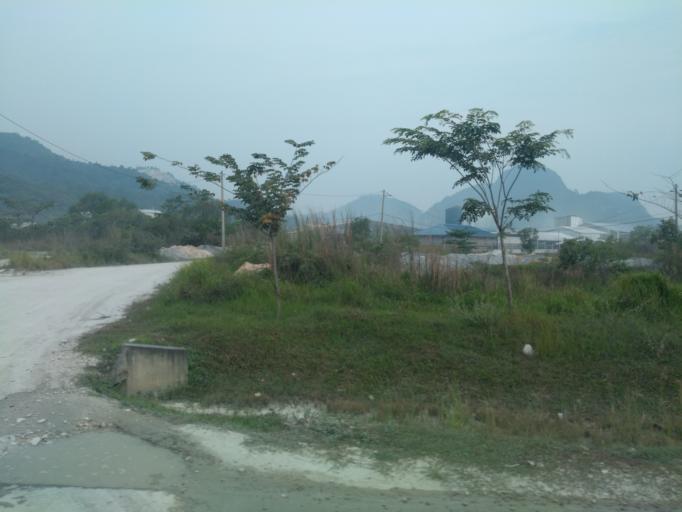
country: MY
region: Perak
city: Ipoh
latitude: 4.5423
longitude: 101.1524
